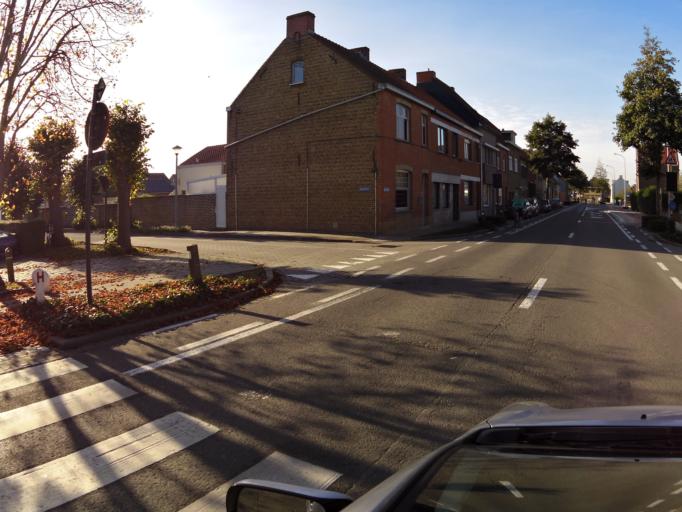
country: BE
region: Flanders
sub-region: Provincie West-Vlaanderen
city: Veurne
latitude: 51.0762
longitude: 2.6761
